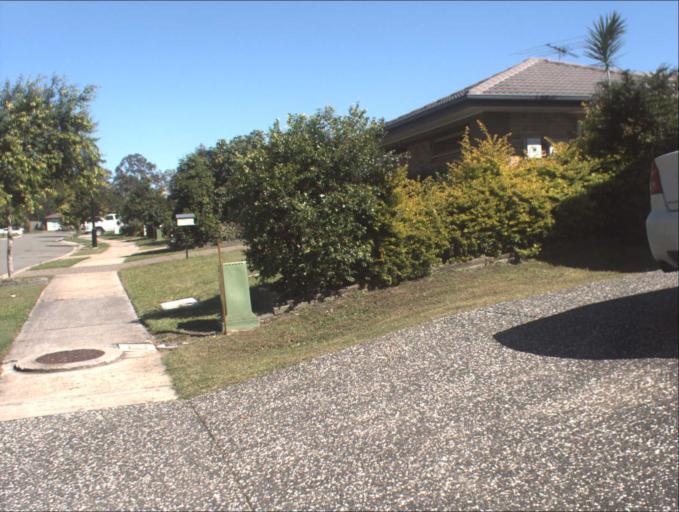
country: AU
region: Queensland
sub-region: Logan
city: Windaroo
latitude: -27.7217
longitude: 153.1696
